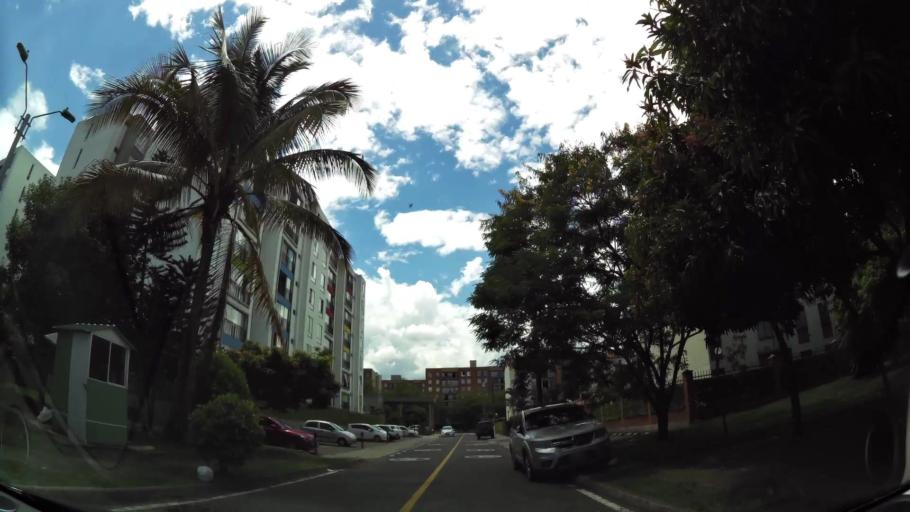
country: CO
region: Valle del Cauca
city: Cali
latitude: 3.3850
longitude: -76.5154
